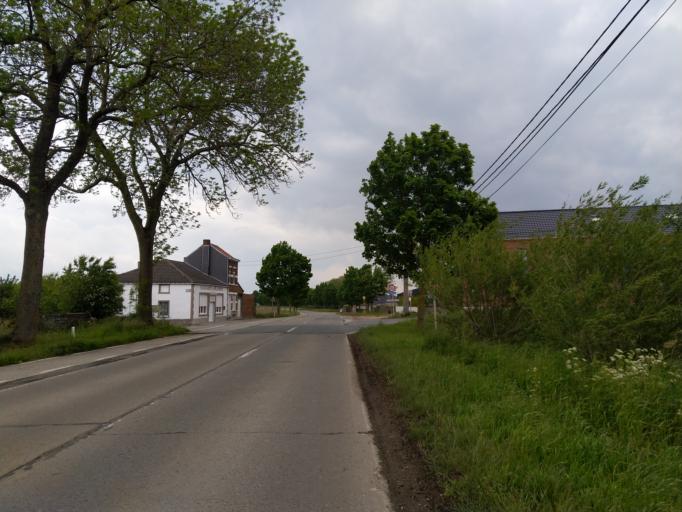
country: BE
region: Wallonia
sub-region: Province du Hainaut
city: Ecaussinnes-d'Enghien
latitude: 50.5790
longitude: 4.1474
